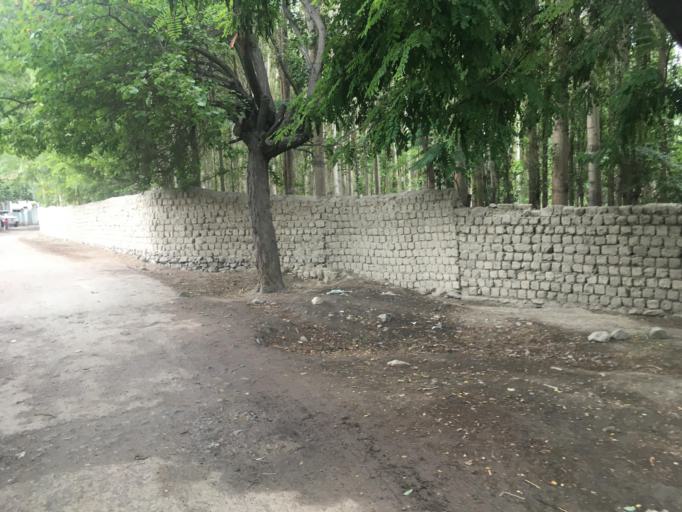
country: PK
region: Gilgit-Baltistan
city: Skardu
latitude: 35.2914
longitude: 75.6507
